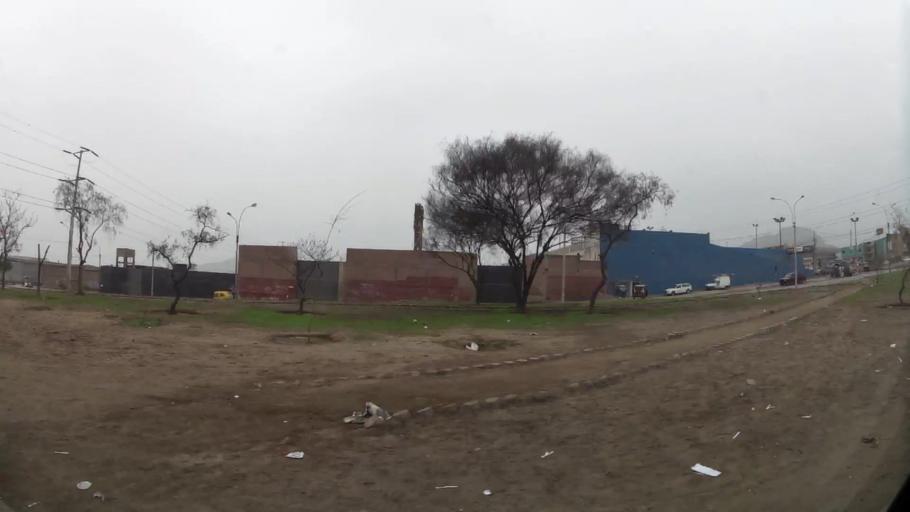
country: PE
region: Lima
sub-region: Lima
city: Surco
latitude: -12.1958
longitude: -76.9356
